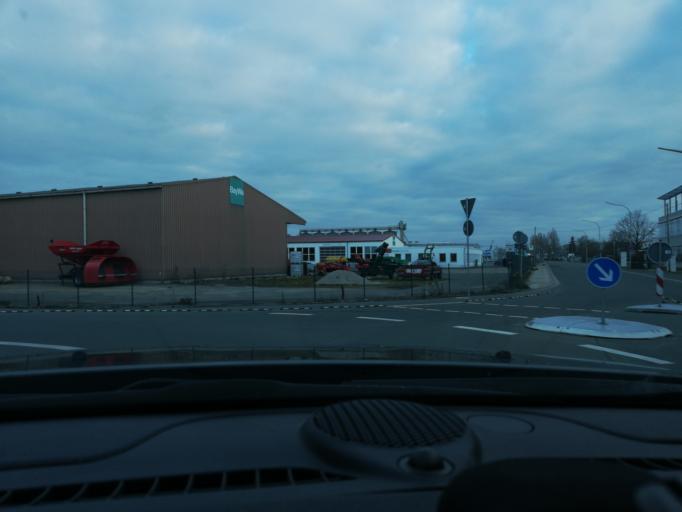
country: DE
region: Bavaria
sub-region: Upper Franconia
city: Forchheim
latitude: 49.7033
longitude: 11.0559
